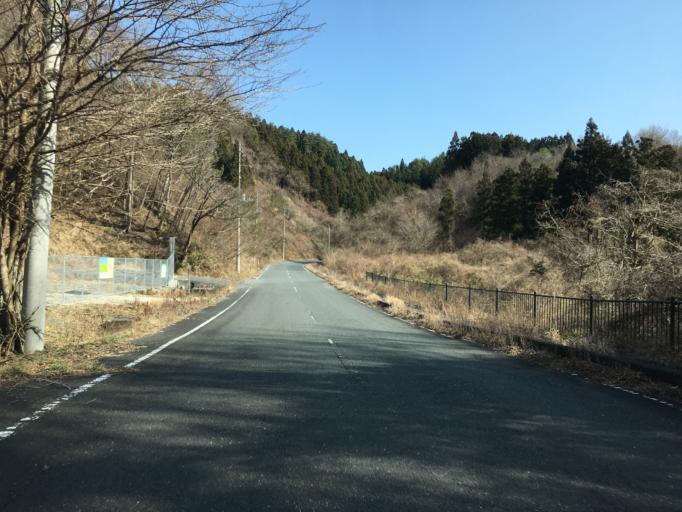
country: JP
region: Ibaraki
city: Kitaibaraki
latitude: 36.8039
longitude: 140.6395
